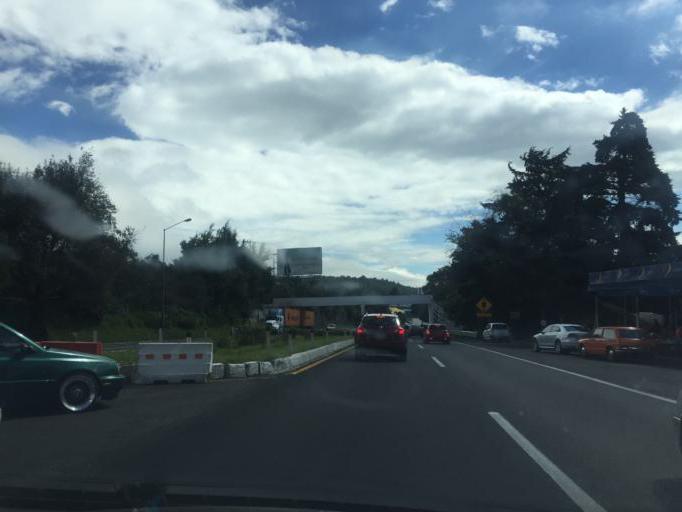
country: MX
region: Morelos
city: Tres Marias
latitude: 19.0321
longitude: -99.2067
